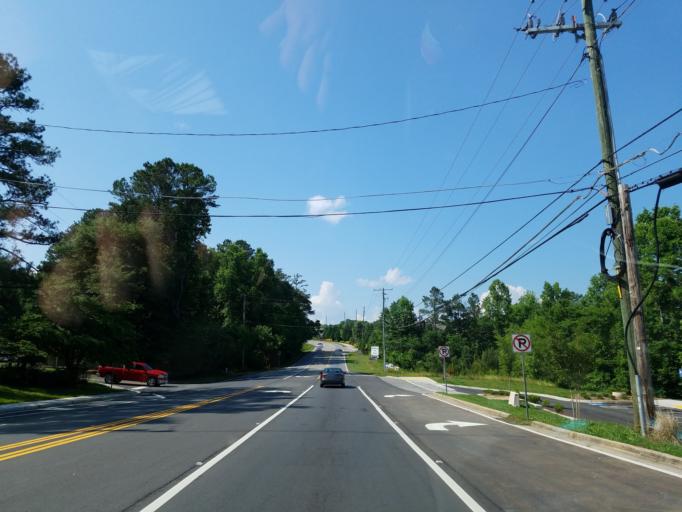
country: US
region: Georgia
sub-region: Cherokee County
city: Woodstock
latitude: 34.1316
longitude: -84.4977
